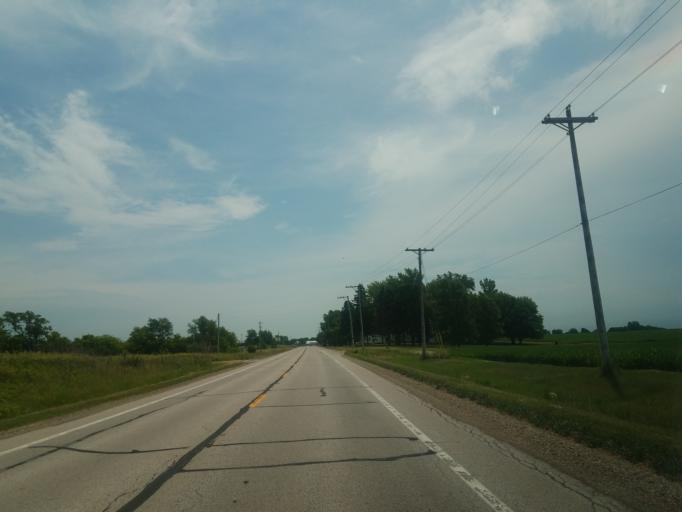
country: US
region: Illinois
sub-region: McLean County
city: Downs
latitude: 40.4297
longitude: -88.9208
